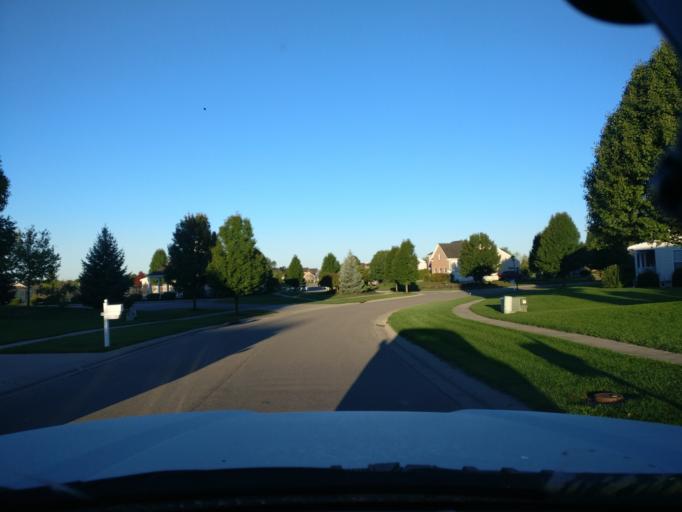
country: US
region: Ohio
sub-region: Warren County
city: Hunter
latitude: 39.4895
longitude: -84.2684
